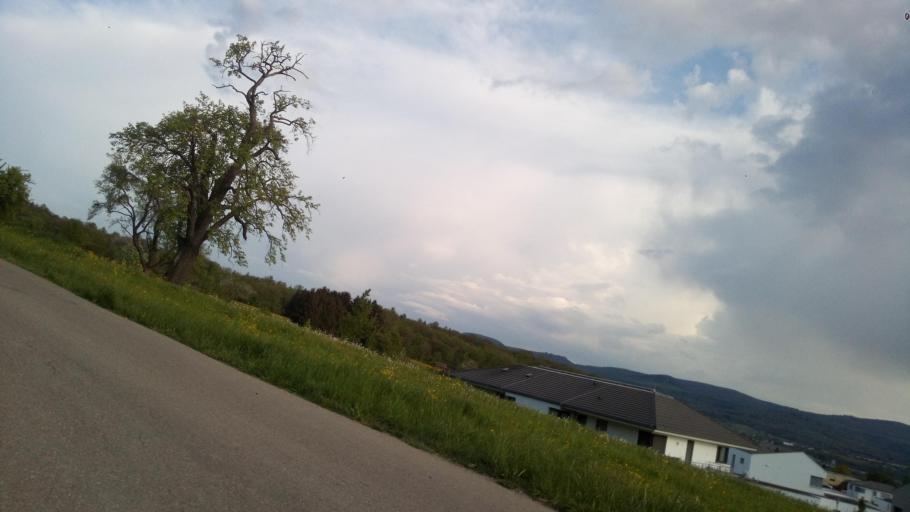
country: DE
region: Baden-Wuerttemberg
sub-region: Regierungsbezirk Stuttgart
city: Salach
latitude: 48.6996
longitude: 9.7503
